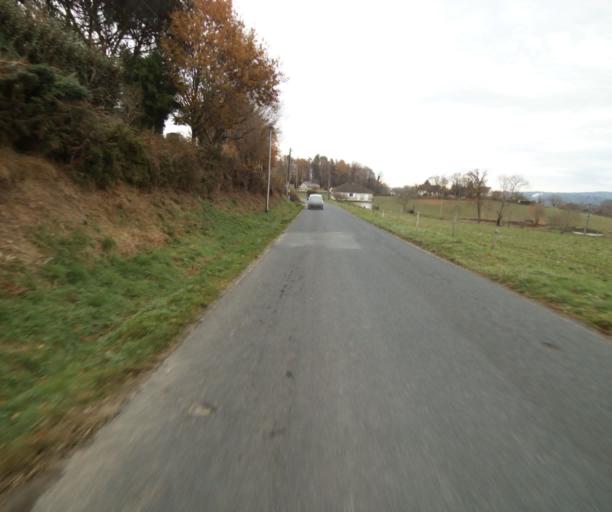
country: FR
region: Limousin
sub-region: Departement de la Correze
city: Tulle
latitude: 45.2632
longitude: 1.7318
